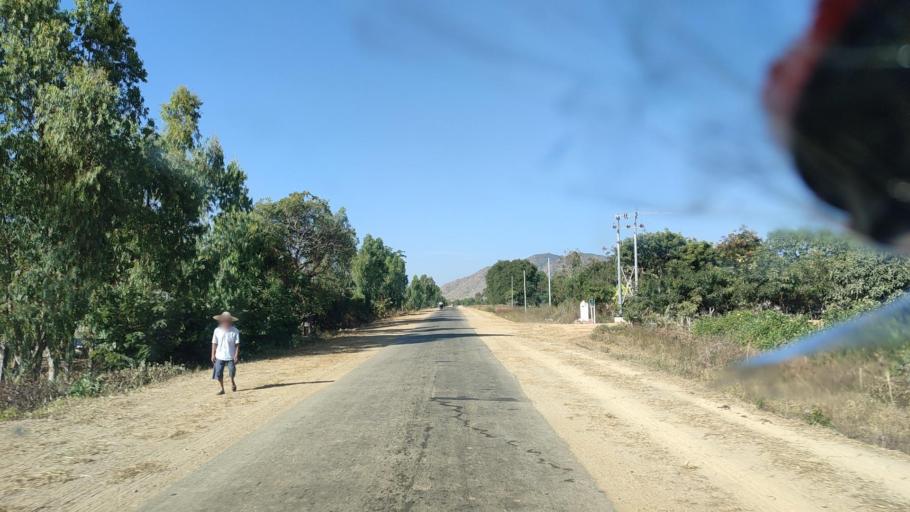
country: MM
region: Mandalay
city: Yamethin
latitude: 20.2326
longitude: 96.2619
